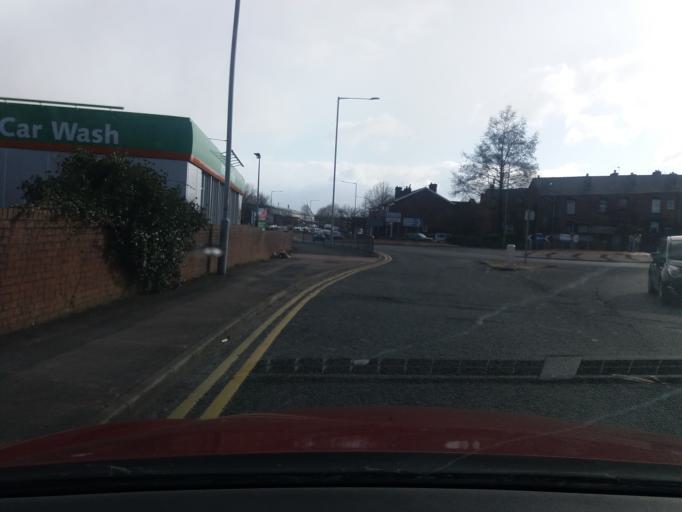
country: GB
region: England
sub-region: Lancashire
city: Chorley
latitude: 53.6612
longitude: -2.6285
